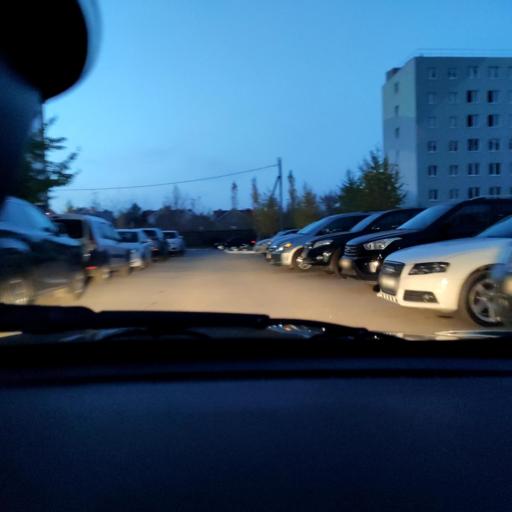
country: RU
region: Samara
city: Tol'yatti
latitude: 53.5311
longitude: 49.3902
